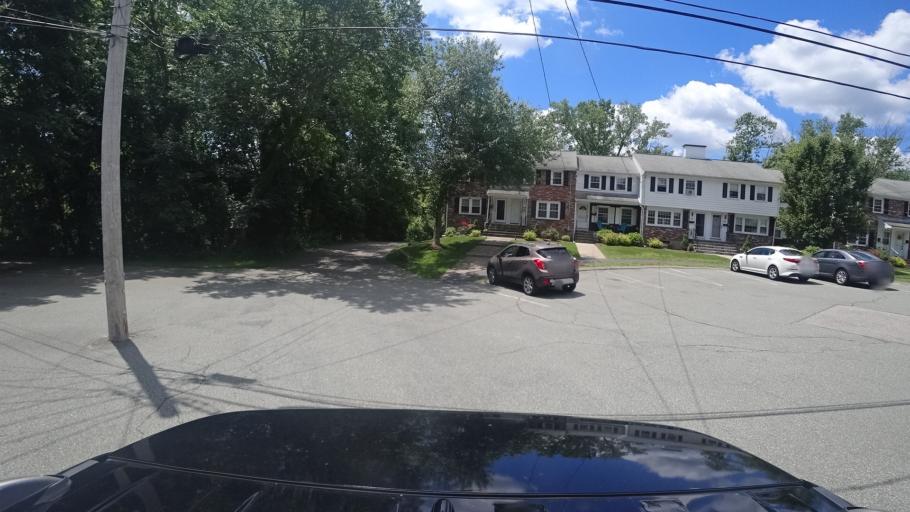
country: US
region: Massachusetts
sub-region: Norfolk County
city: Dedham
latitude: 42.2552
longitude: -71.1752
